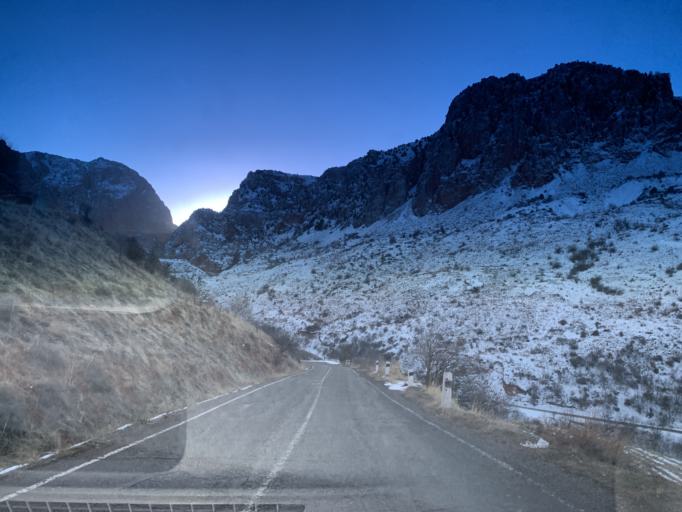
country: AM
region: Vayots' Dzori Marz
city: Areni
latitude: 39.6840
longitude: 45.2318
